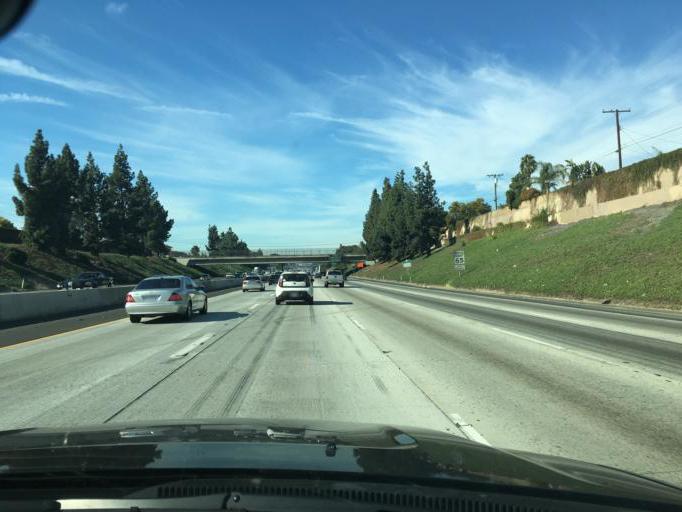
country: US
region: California
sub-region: San Bernardino County
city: Chino
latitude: 34.0304
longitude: -117.6779
